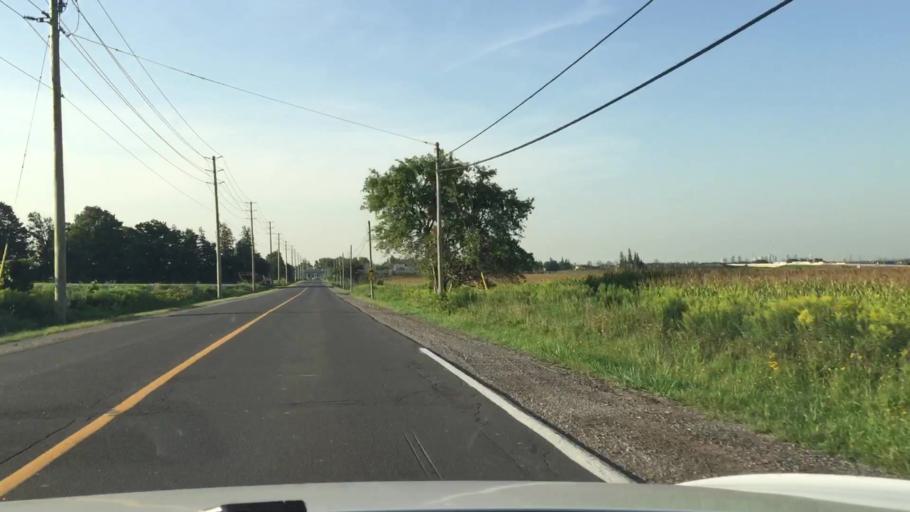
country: CA
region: Ontario
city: Markham
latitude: 43.8825
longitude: -79.2101
